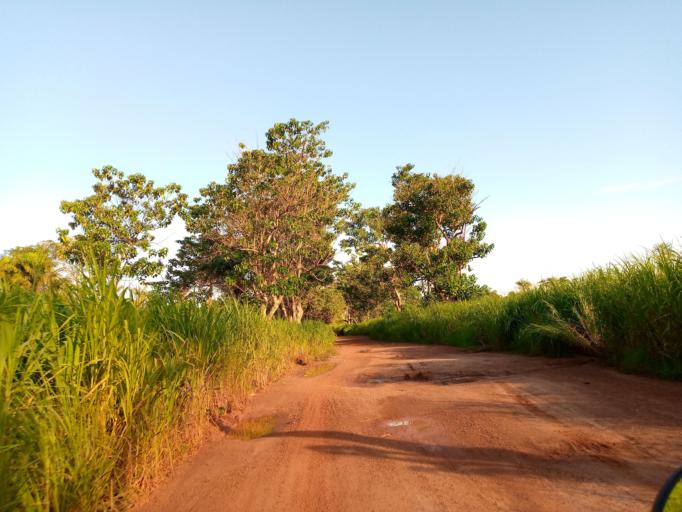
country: SL
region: Northern Province
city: Yonibana
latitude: 8.4530
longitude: -12.2452
